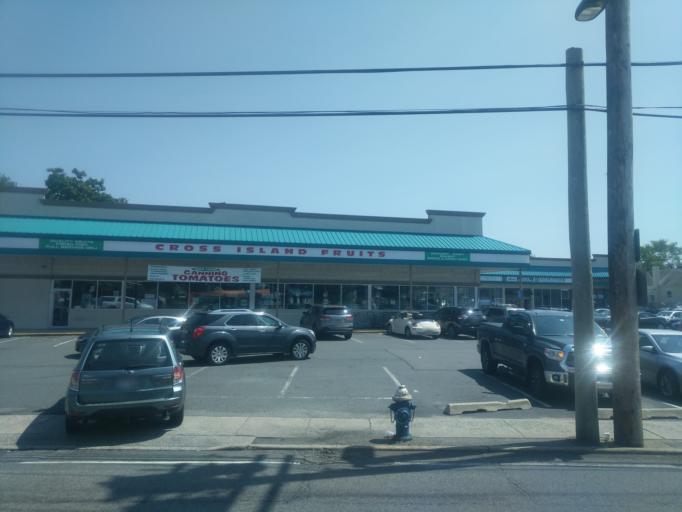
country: US
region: New York
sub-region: Nassau County
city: Lynbrook
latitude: 40.6665
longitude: -73.6706
